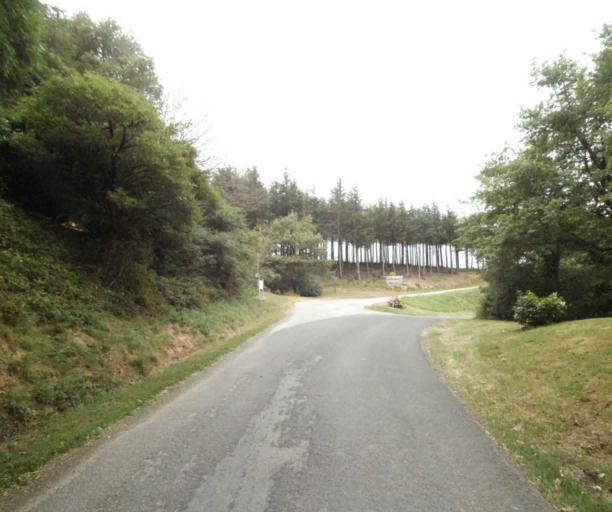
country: FR
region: Midi-Pyrenees
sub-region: Departement du Tarn
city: Soreze
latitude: 43.4123
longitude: 2.0543
